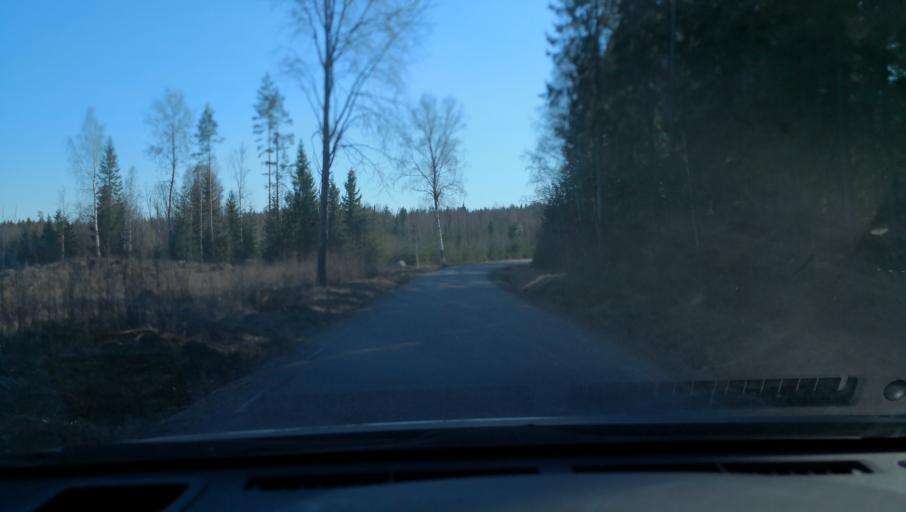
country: SE
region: Dalarna
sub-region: Avesta Kommun
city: Horndal
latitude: 60.0782
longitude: 16.3930
